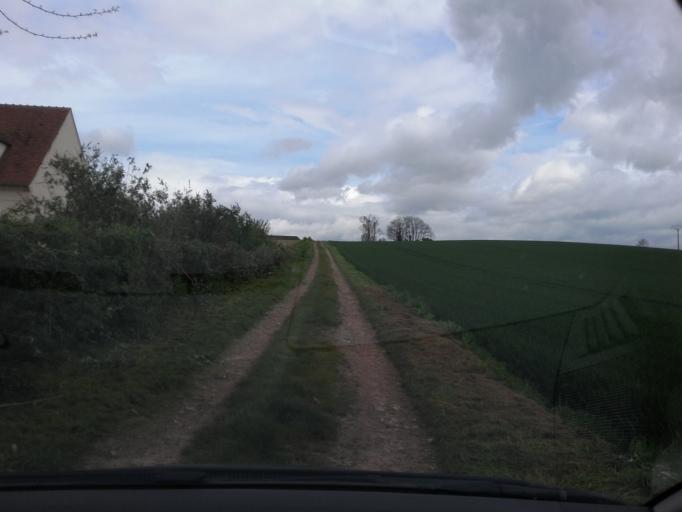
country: FR
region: Picardie
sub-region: Departement de l'Oise
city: Grandfresnoy
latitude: 49.3669
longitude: 2.6628
